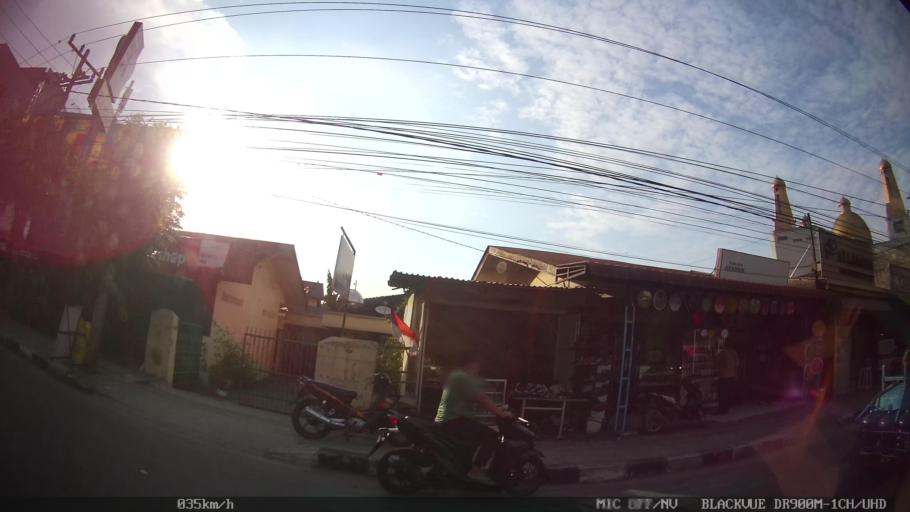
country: ID
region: North Sumatra
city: Sunggal
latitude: 3.5668
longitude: 98.6414
